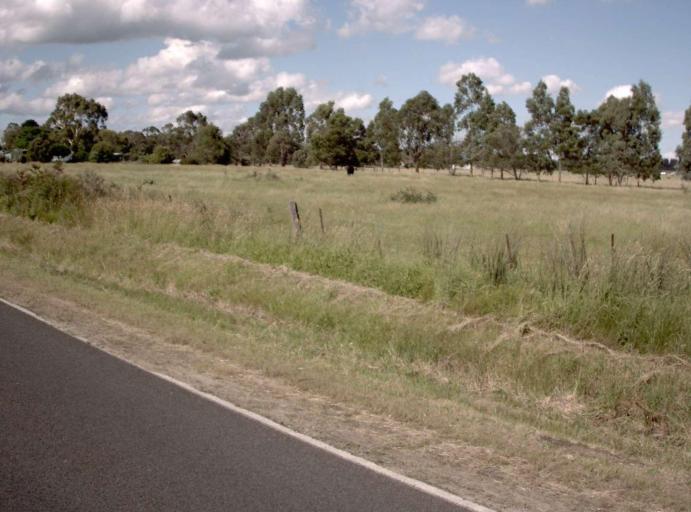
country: AU
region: Victoria
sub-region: Latrobe
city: Morwell
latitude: -38.2098
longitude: 146.3999
